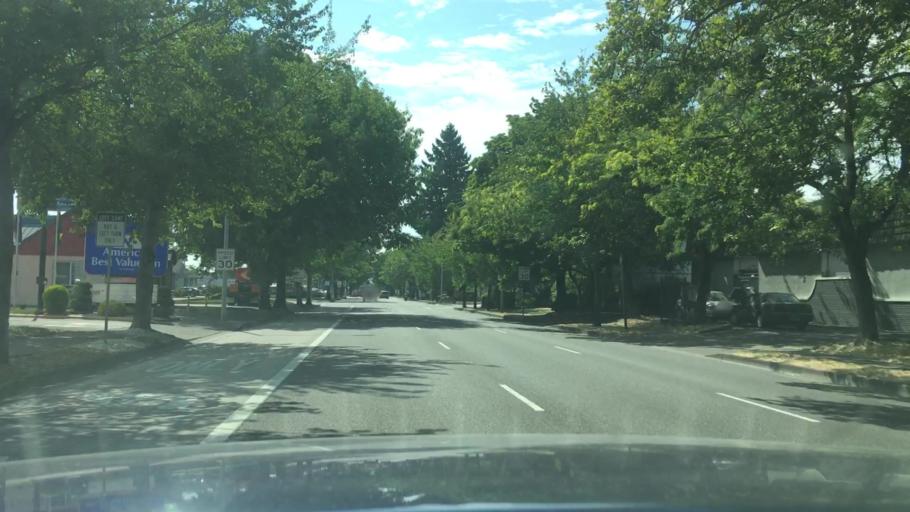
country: US
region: Oregon
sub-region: Lane County
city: Eugene
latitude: 44.0533
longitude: -123.1097
